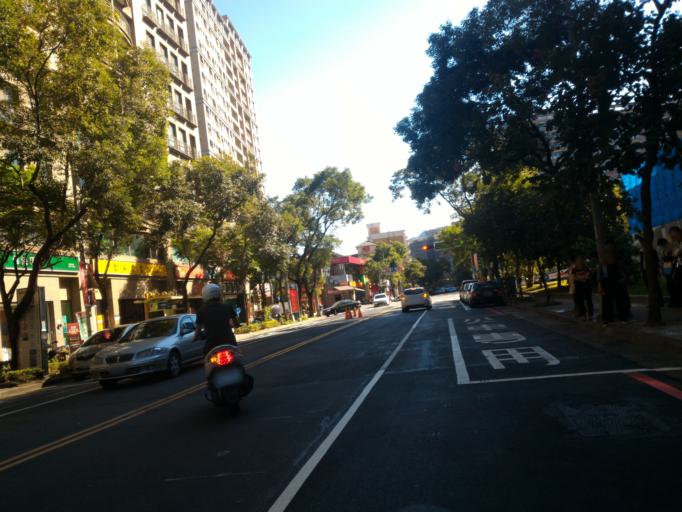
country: TW
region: Taiwan
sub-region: Taoyuan
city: Taoyuan
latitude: 24.9433
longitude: 121.3751
